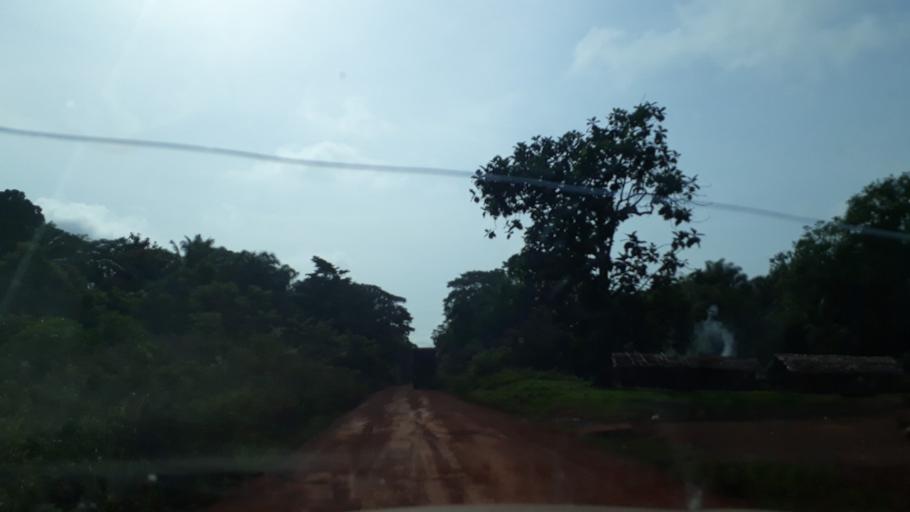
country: CD
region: Eastern Province
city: Wamba
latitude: 1.4027
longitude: 27.6599
